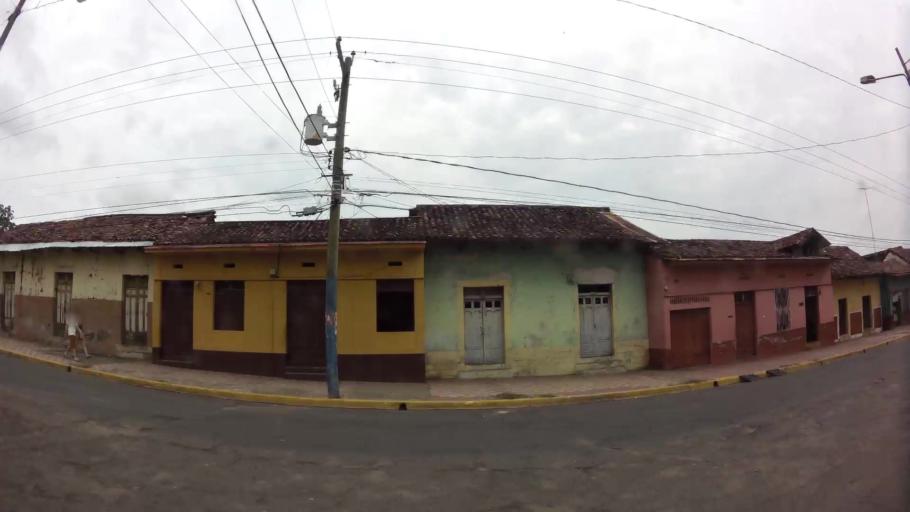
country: NI
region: Granada
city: Granada
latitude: 11.9284
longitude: -85.9632
